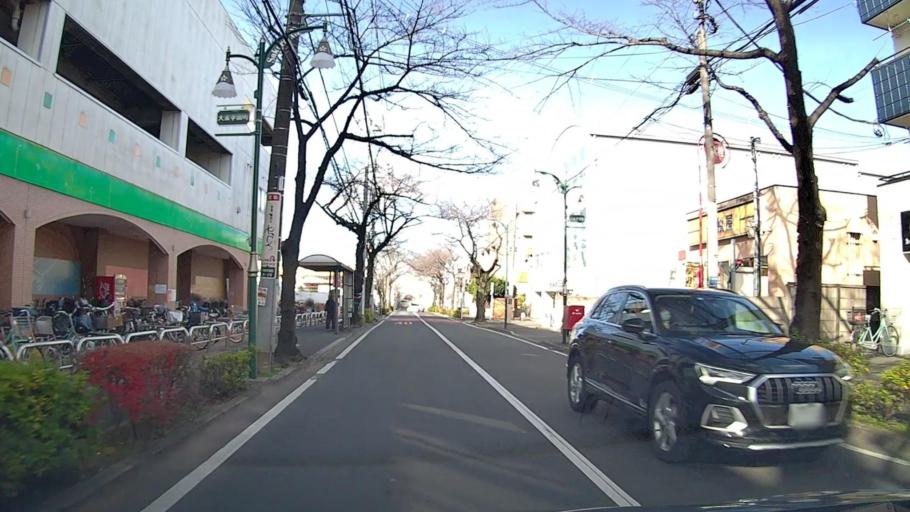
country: JP
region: Saitama
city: Asaka
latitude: 35.7735
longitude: 139.5863
